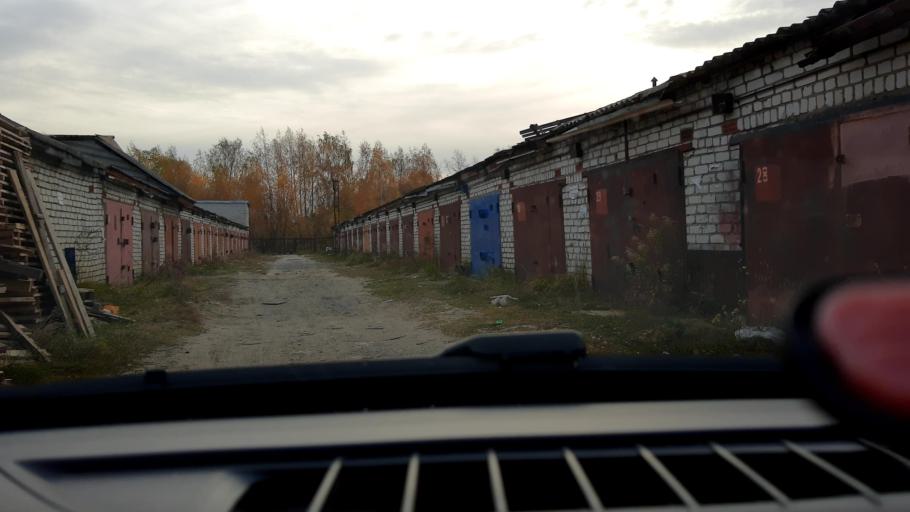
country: RU
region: Nizjnij Novgorod
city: Gorbatovka
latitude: 56.3320
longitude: 43.8168
